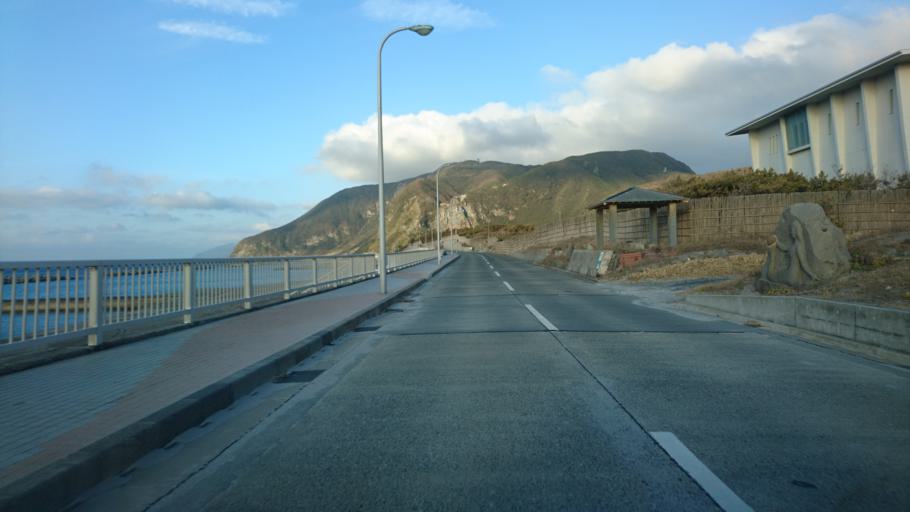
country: JP
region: Shizuoka
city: Shimoda
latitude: 34.3735
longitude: 139.2511
